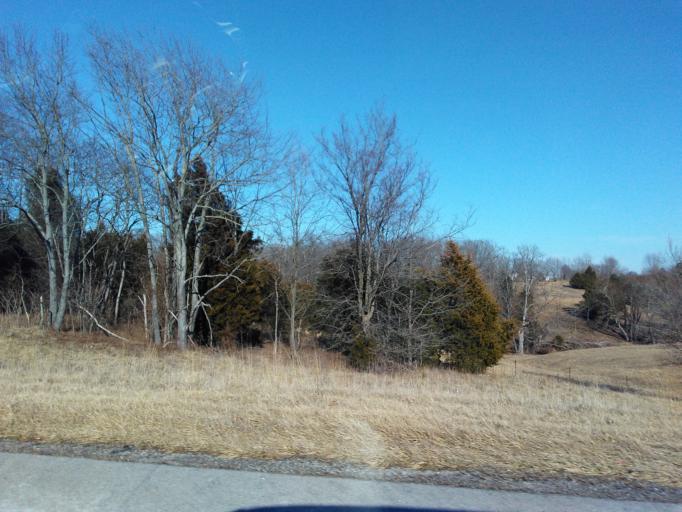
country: US
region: Illinois
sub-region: Johnson County
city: Goreville
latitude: 37.5722
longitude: -88.9572
